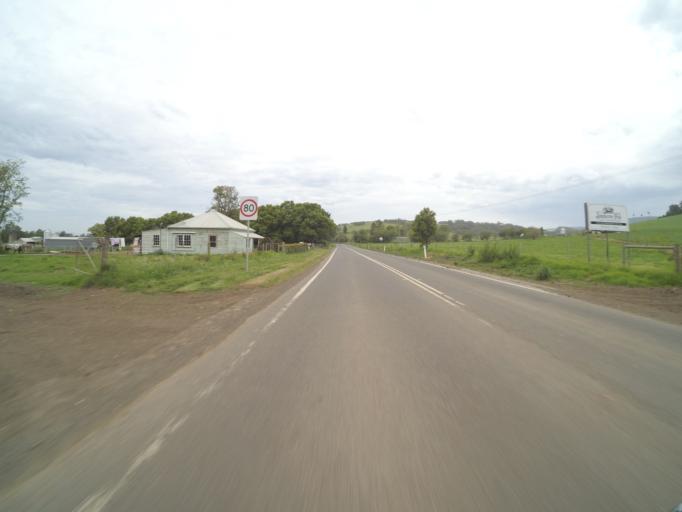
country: AU
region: New South Wales
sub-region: Kiama
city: Jamberoo
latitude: -34.6501
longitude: 150.7918
